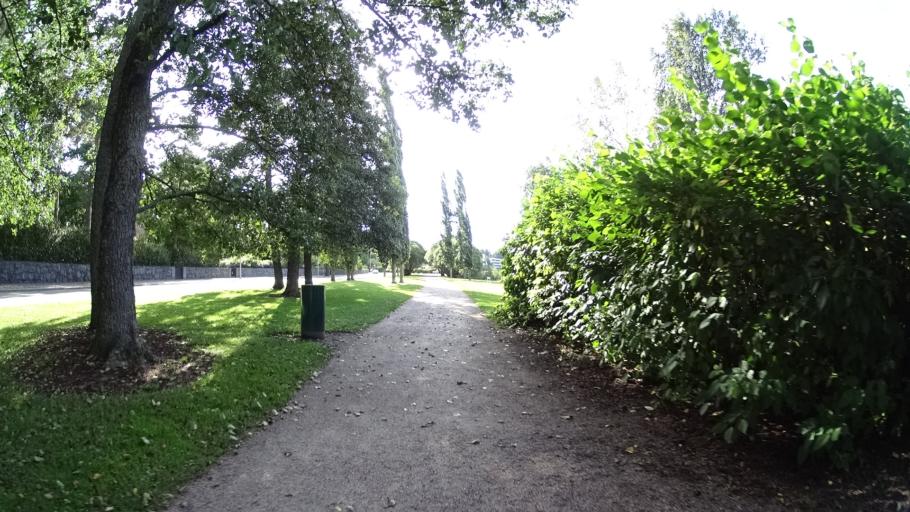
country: FI
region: Uusimaa
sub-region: Helsinki
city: Teekkarikylae
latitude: 60.1961
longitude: 24.8694
